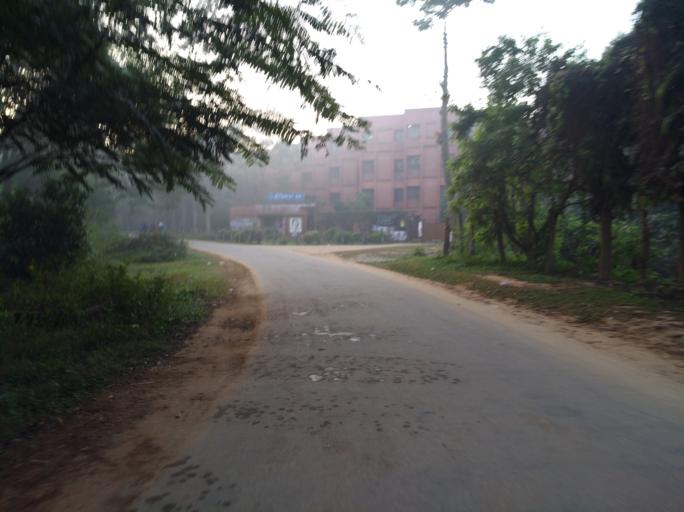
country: BD
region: Dhaka
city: Tungi
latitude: 23.8852
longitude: 90.2707
